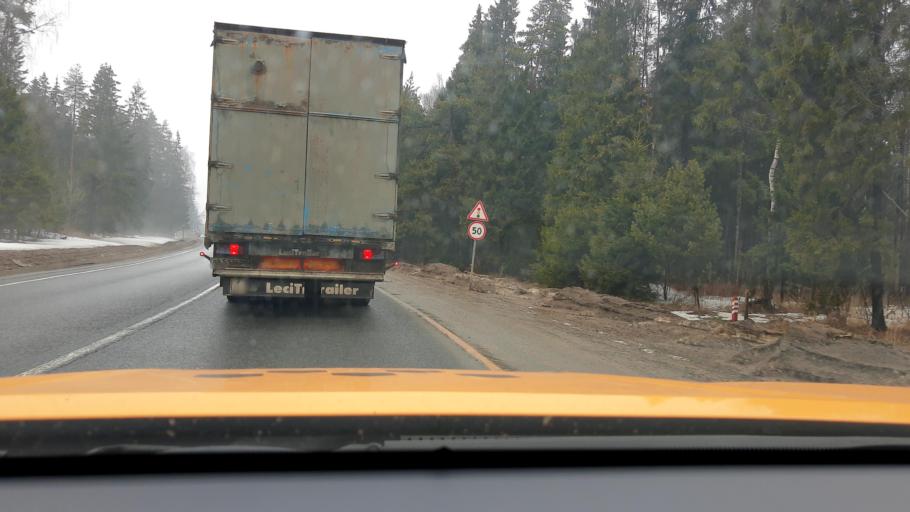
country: RU
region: Moskovskaya
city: Chernogolovka
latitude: 55.9827
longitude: 38.3433
